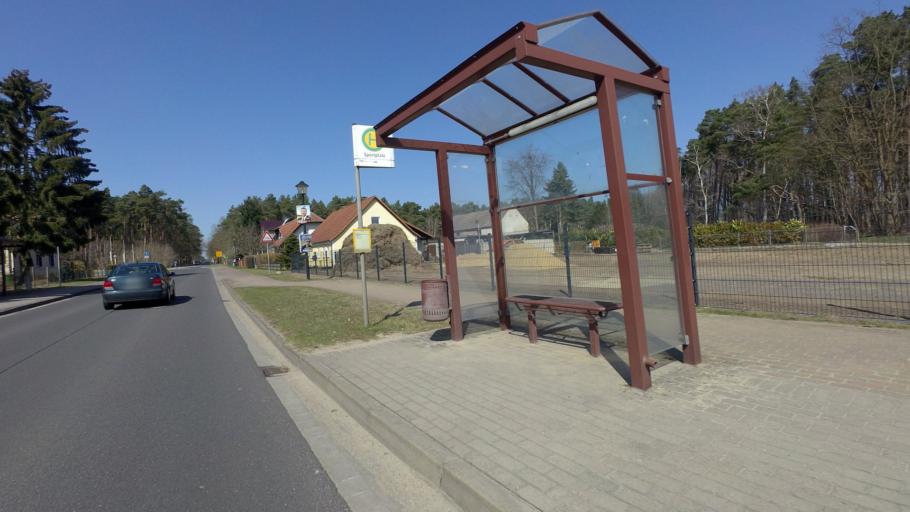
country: DE
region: Brandenburg
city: Ruthnick
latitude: 52.9072
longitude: 12.9600
